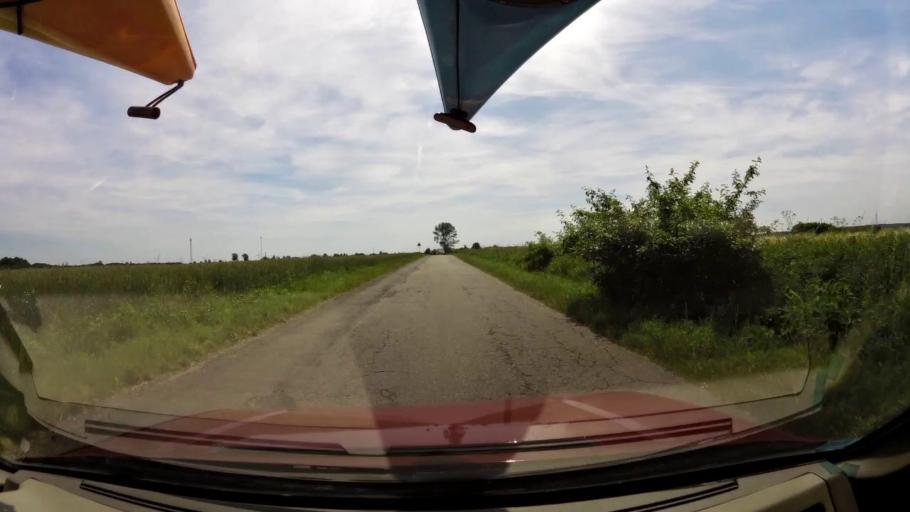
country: PL
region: West Pomeranian Voivodeship
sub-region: Powiat slawienski
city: Darlowo
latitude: 54.3245
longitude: 16.3947
